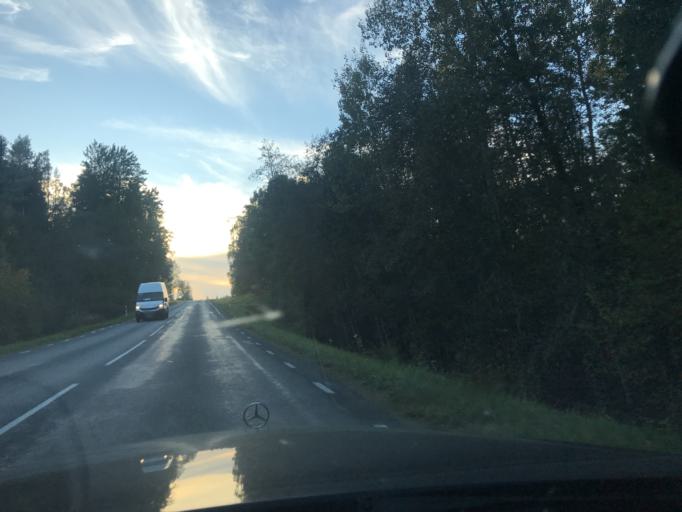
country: EE
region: Vorumaa
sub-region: Antsla vald
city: Vana-Antsla
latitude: 57.8788
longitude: 26.6831
